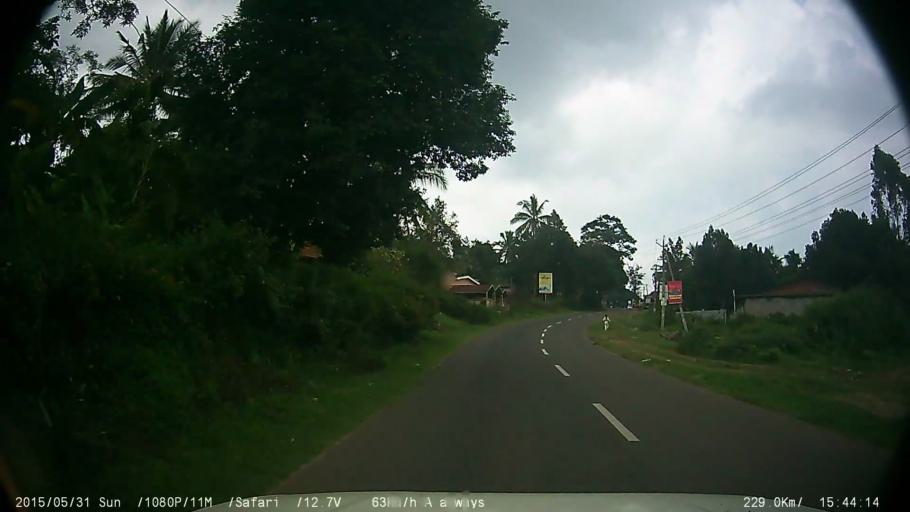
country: IN
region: Kerala
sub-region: Wayanad
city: Panamaram
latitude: 11.6732
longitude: 76.2855
